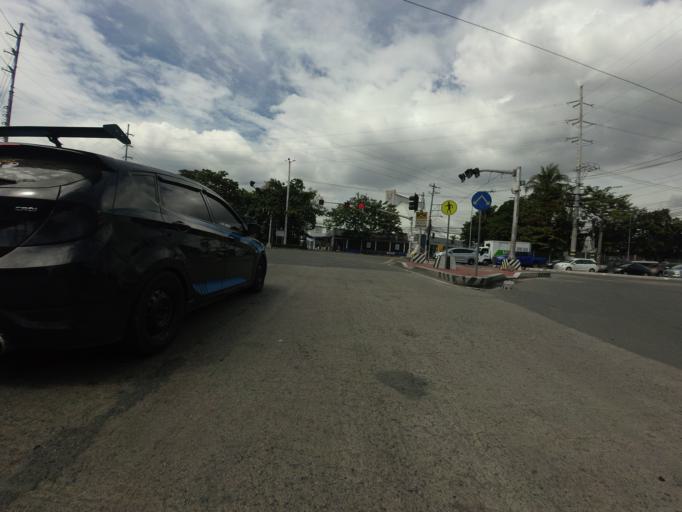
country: PH
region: Metro Manila
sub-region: City of Manila
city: Quiapo
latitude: 14.5854
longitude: 120.9941
